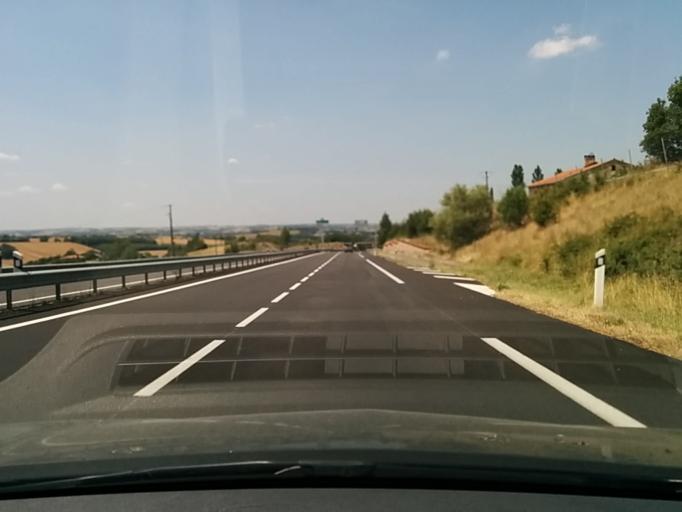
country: FR
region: Midi-Pyrenees
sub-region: Departement du Gers
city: Pujaudran
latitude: 43.5956
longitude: 1.1165
